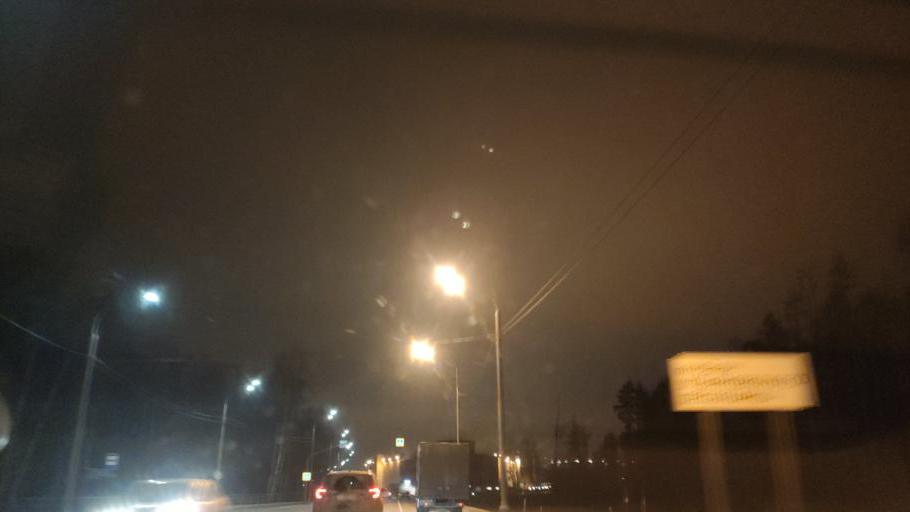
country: RU
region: Moskovskaya
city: Moskovskiy
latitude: 55.6121
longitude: 37.3495
